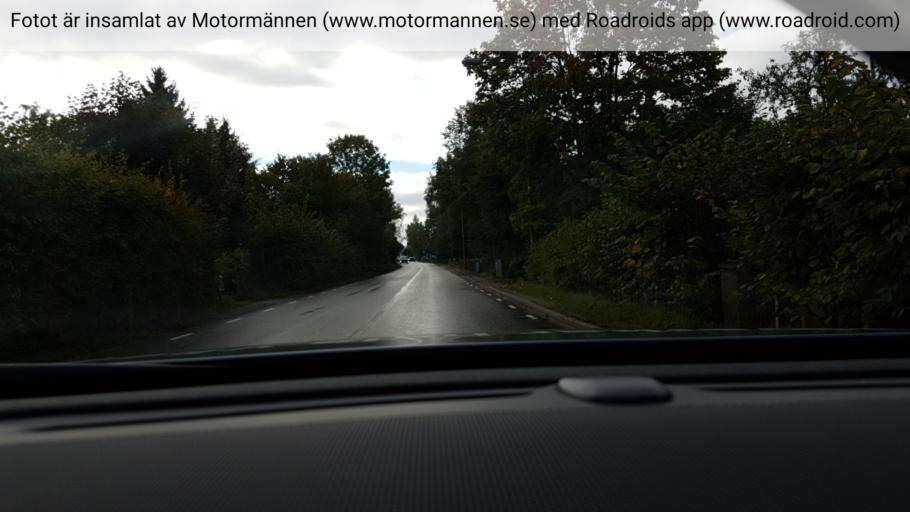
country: SE
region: Vaestra Goetaland
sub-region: Marks Kommun
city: Kinna
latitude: 57.4778
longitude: 12.7046
